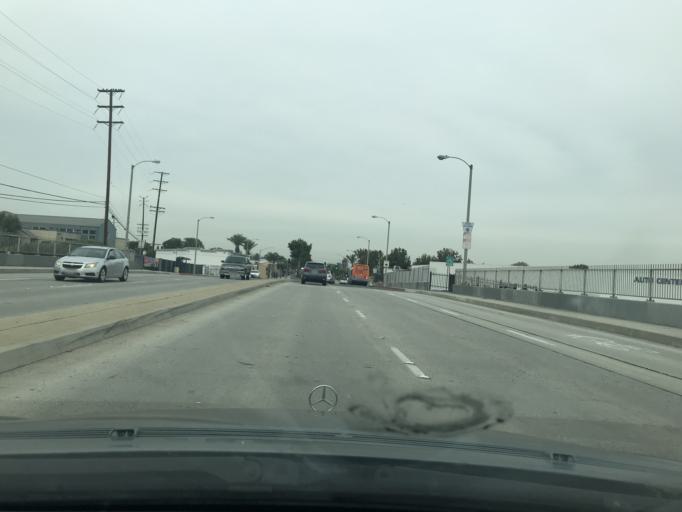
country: US
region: California
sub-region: Los Angeles County
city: Bell Gardens
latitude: 33.9607
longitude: -118.1439
